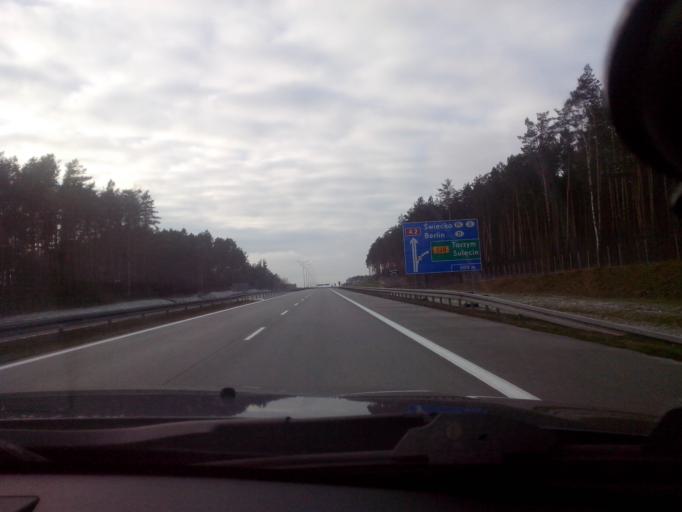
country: PL
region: Lubusz
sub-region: Powiat sulecinski
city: Torzym
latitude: 52.3256
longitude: 15.1002
